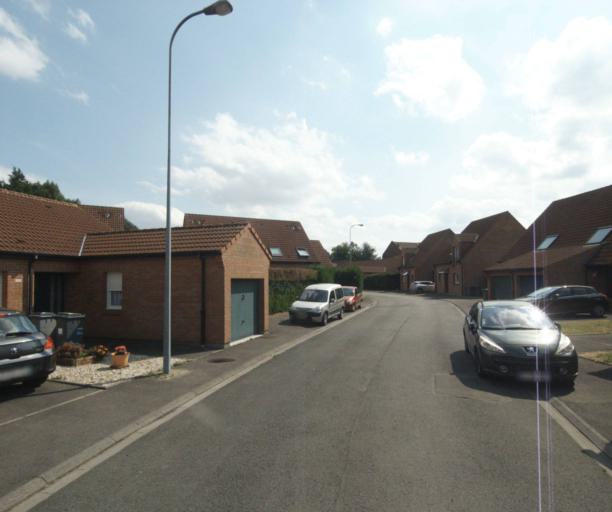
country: FR
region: Nord-Pas-de-Calais
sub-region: Departement du Nord
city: Lannoy
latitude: 50.6645
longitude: 3.2033
